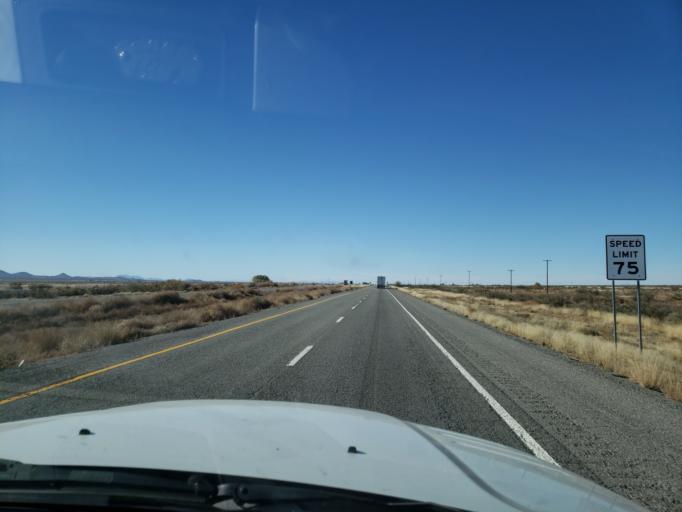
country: US
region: New Mexico
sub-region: Hidalgo County
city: Lordsburg
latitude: 32.3163
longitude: -108.6143
